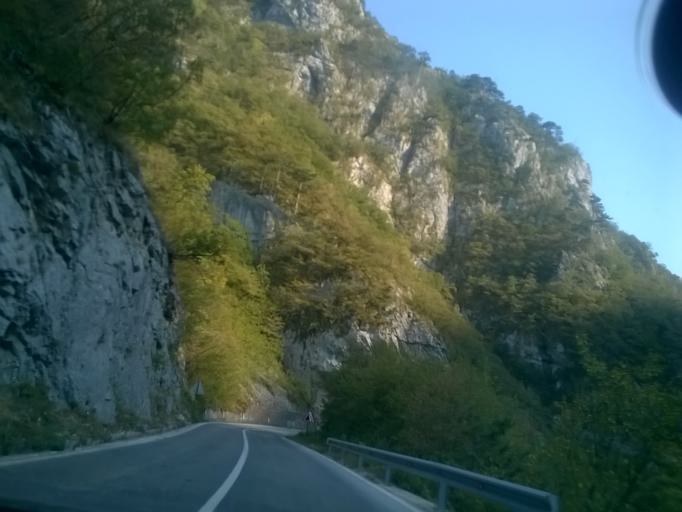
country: ME
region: Opstina Pluzine
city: Pluzine
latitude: 43.2286
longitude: 18.8470
